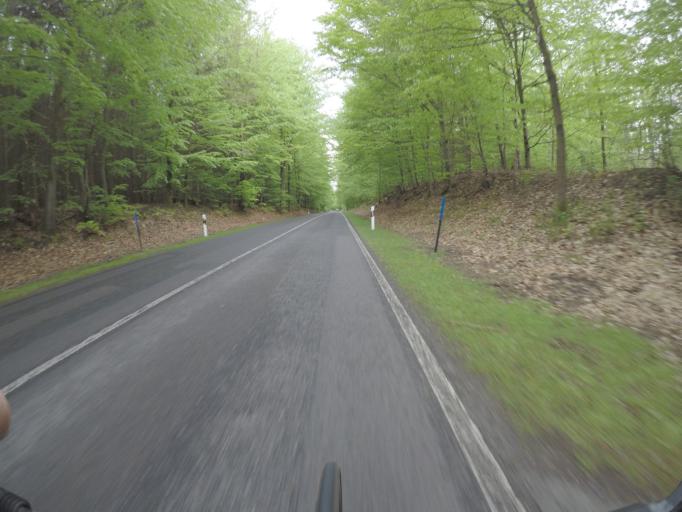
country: DE
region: Brandenburg
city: Joachimsthal
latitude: 52.9386
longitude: 13.7387
